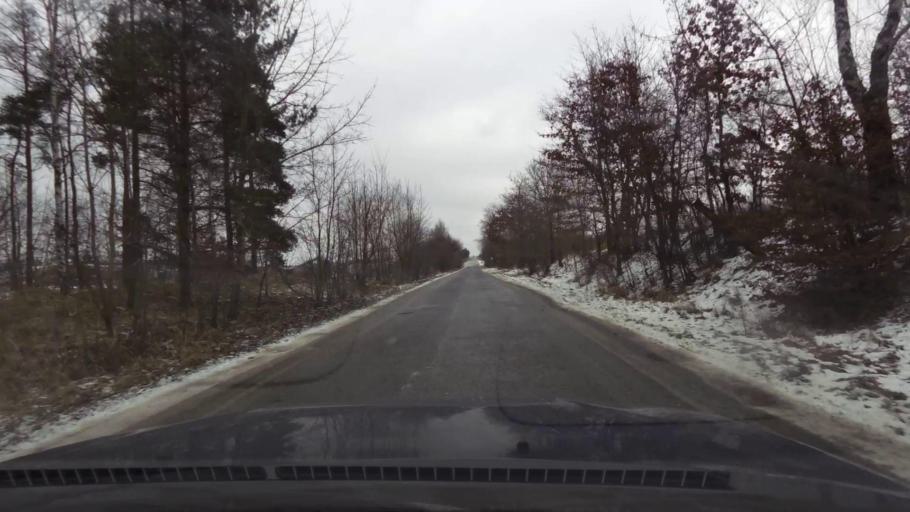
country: PL
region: West Pomeranian Voivodeship
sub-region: Powiat lobeski
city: Wegorzyno
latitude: 53.4870
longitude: 15.6173
